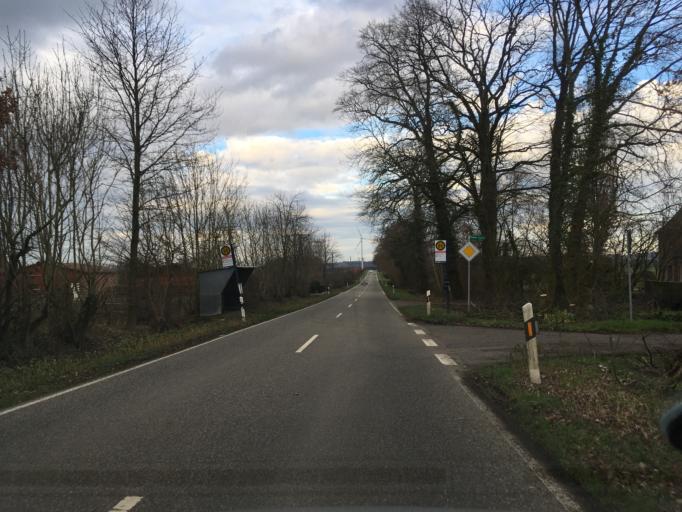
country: DE
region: North Rhine-Westphalia
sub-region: Regierungsbezirk Munster
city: Schoppingen
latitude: 52.0686
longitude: 7.1878
